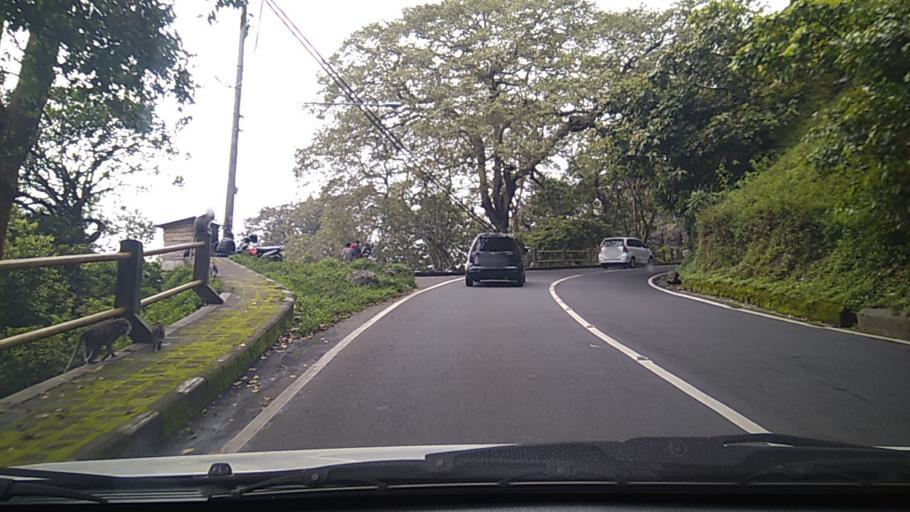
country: ID
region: Bali
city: Munduk
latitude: -8.2382
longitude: 115.1428
